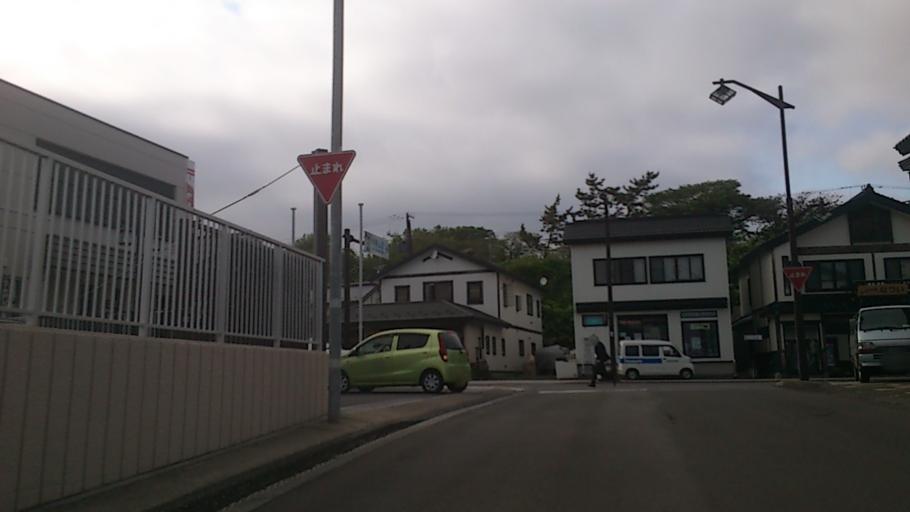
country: JP
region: Hokkaido
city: Kamiiso
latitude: 41.4282
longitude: 140.1092
